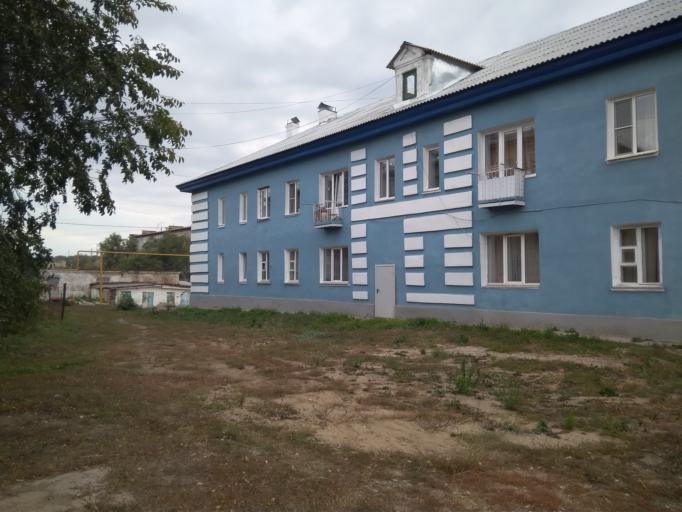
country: RU
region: Chelyabinsk
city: Troitsk
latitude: 54.0905
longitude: 61.5545
